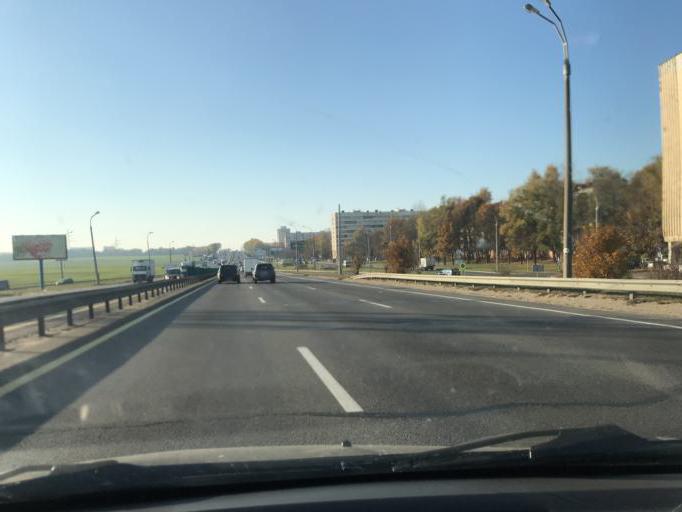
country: BY
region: Minsk
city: Yubilyeyny
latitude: 53.8388
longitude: 27.5021
